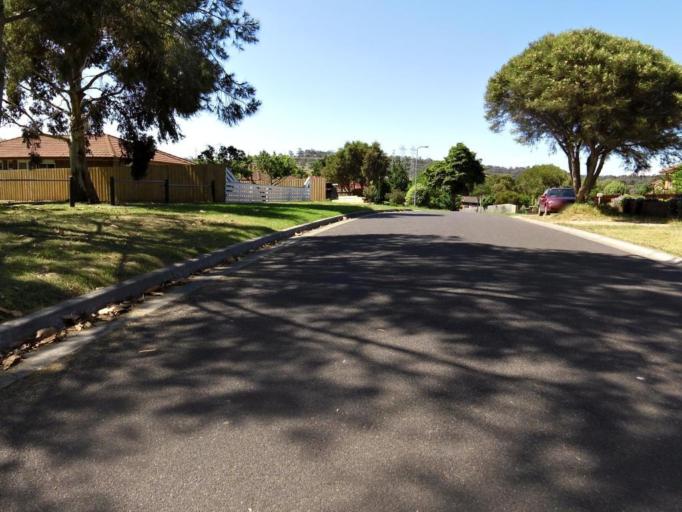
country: AU
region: Victoria
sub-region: Casey
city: Endeavour Hills
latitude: -37.9647
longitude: 145.2654
